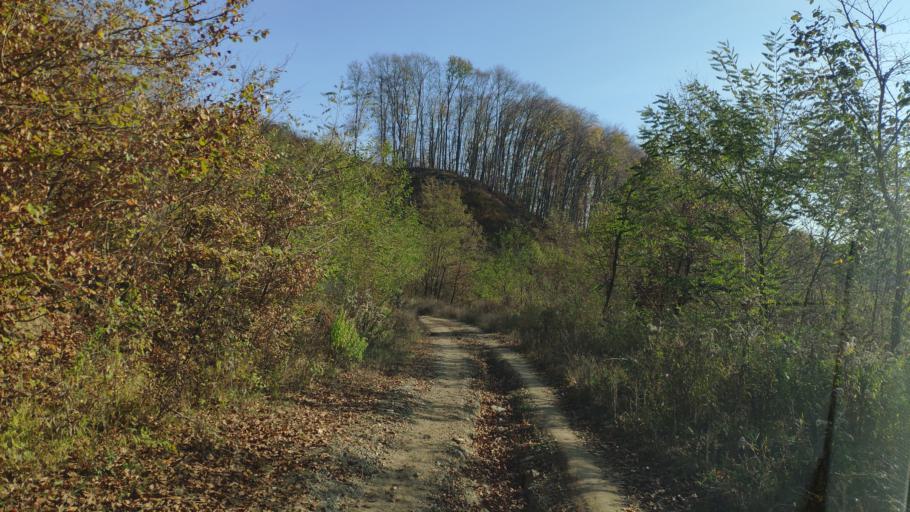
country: SK
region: Presovsky
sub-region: Okres Presov
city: Presov
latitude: 48.9035
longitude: 21.2234
